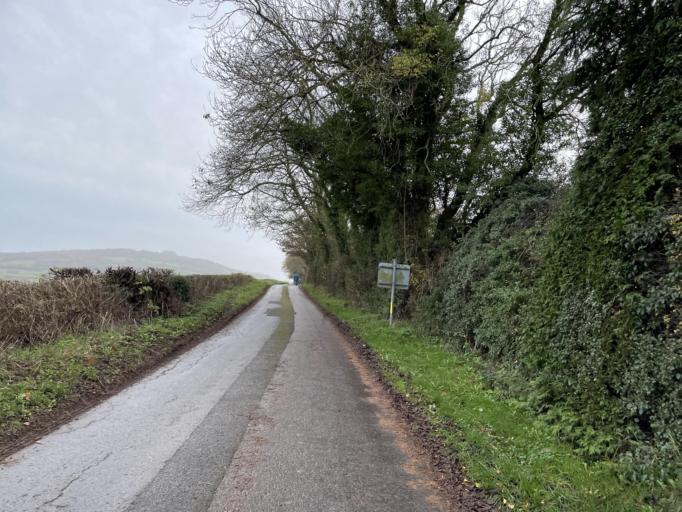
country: GB
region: England
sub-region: Herefordshire
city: Lea
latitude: 51.9165
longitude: -2.4845
